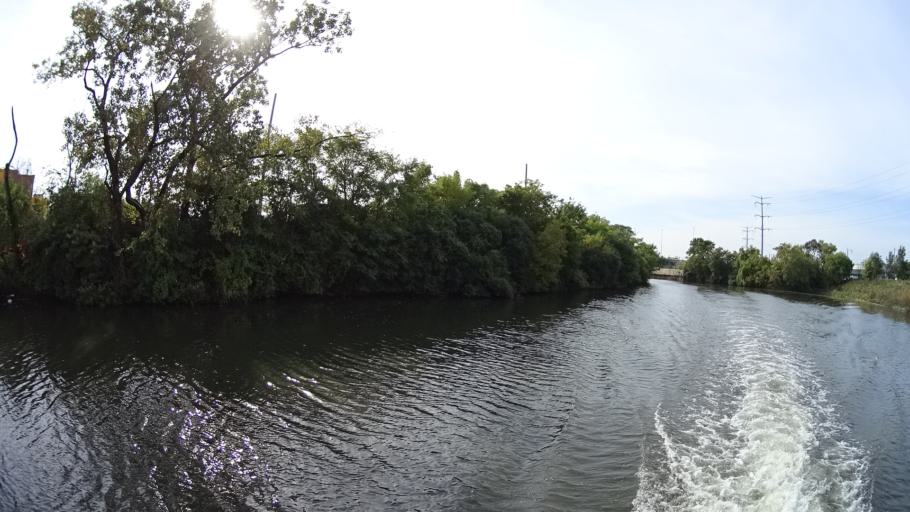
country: US
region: Illinois
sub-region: Cook County
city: Chicago
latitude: 41.8423
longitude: -87.6640
